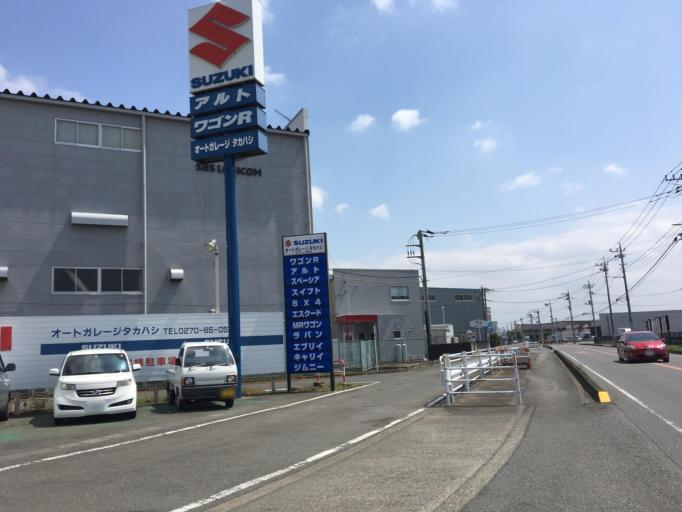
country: JP
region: Gunma
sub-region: Sawa-gun
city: Tamamura
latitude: 36.2973
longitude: 139.1362
